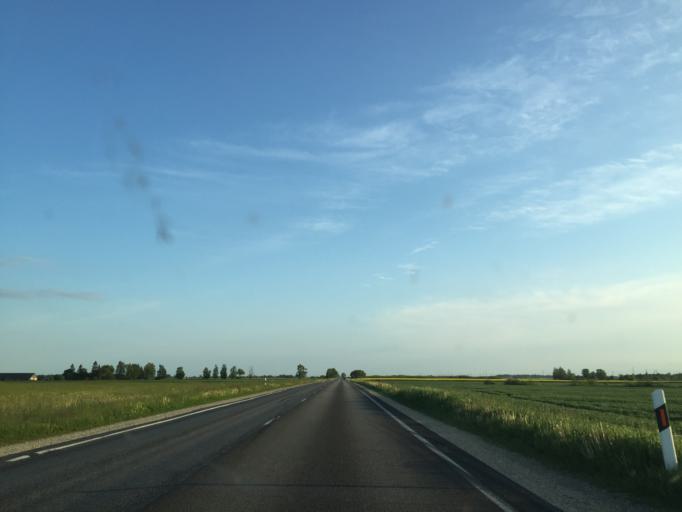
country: LT
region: Siauliu apskritis
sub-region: Joniskis
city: Joniskis
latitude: 56.0947
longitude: 23.4739
